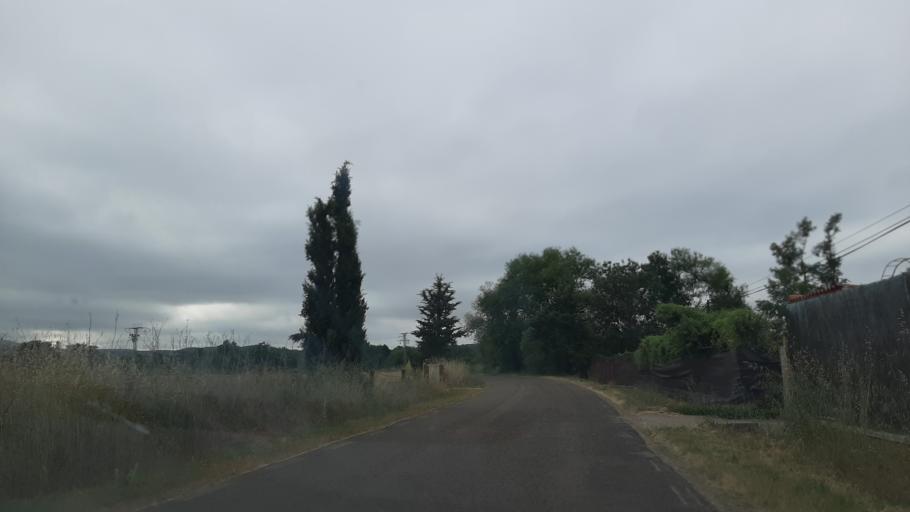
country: ES
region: Castille and Leon
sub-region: Provincia de Salamanca
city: Pastores
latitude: 40.5660
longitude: -6.4872
